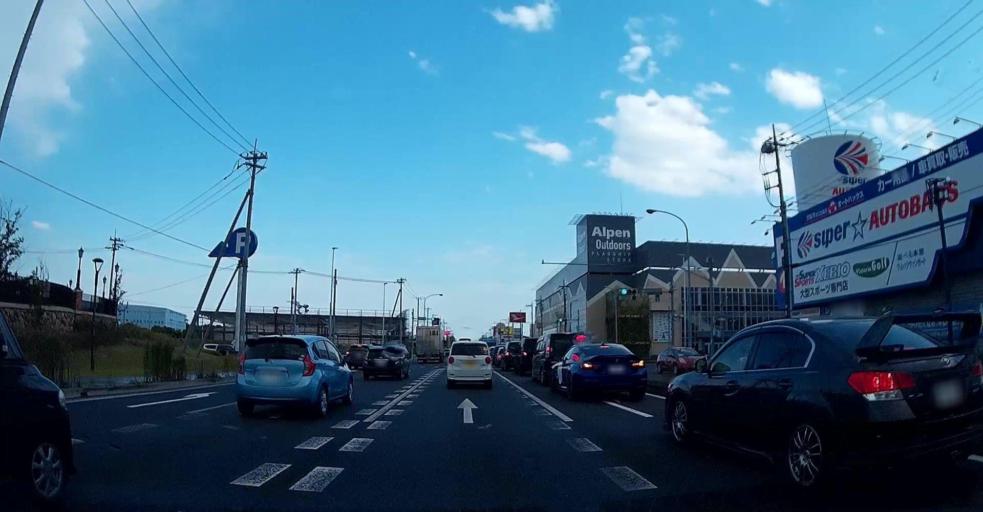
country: JP
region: Chiba
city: Abiko
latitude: 35.8307
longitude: 140.0131
